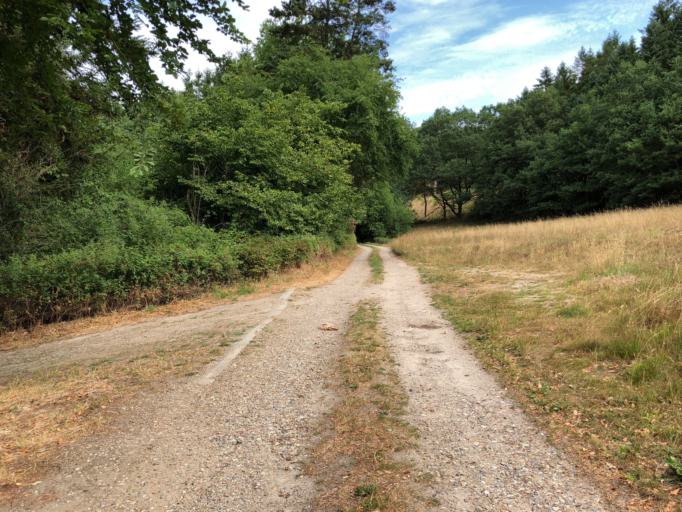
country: DK
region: South Denmark
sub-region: Vejle Kommune
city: Egtved
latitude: 55.6584
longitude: 9.2934
